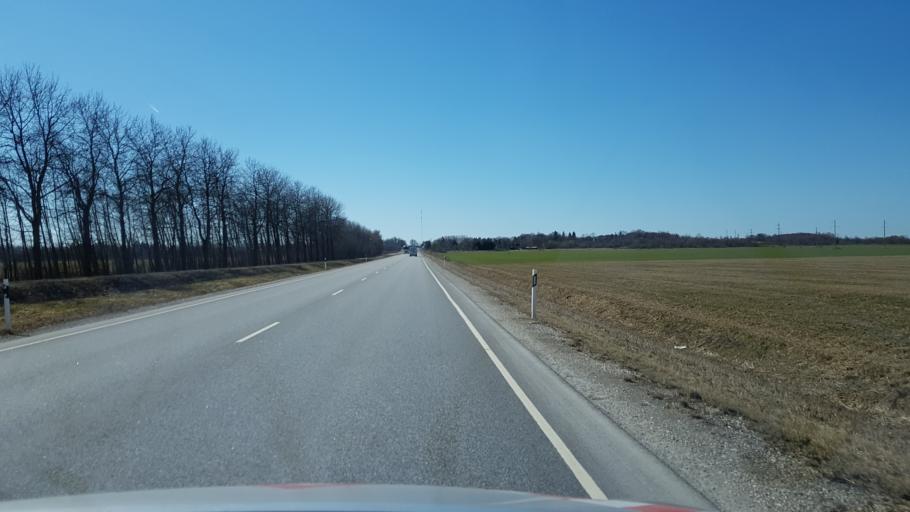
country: EE
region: Laeaene
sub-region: Lihula vald
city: Lihula
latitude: 58.7299
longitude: 23.9711
